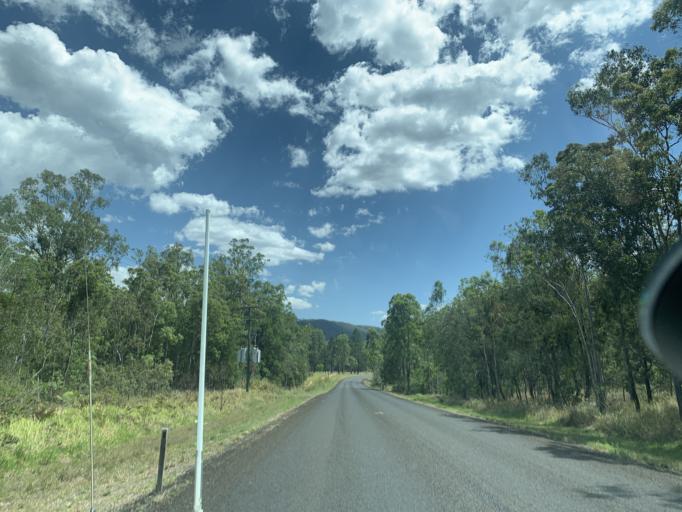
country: AU
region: Queensland
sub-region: Tablelands
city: Atherton
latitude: -17.3158
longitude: 145.4505
